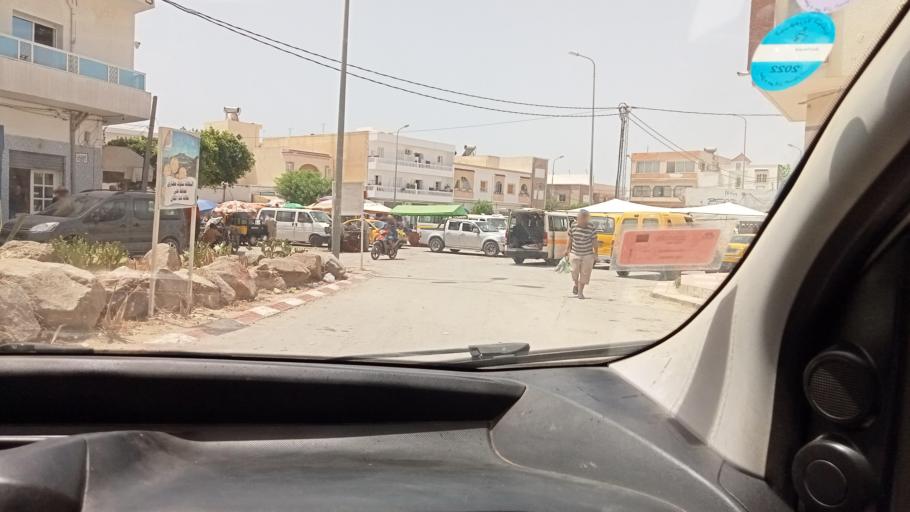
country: TN
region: Nabul
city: Qulaybiyah
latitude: 36.8520
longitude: 11.0896
